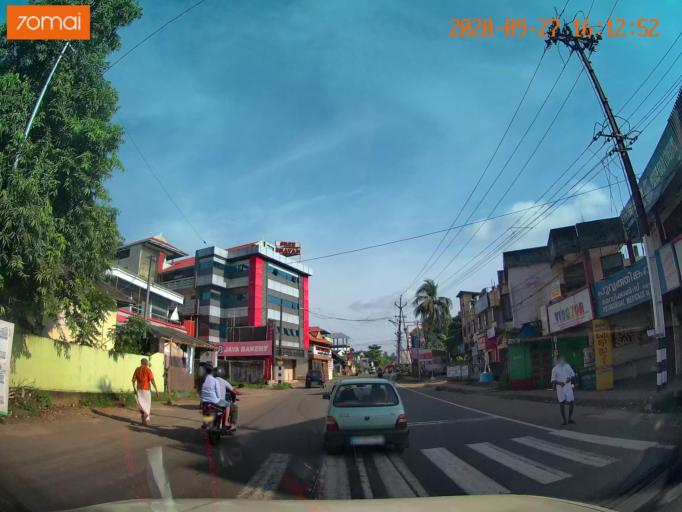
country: IN
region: Kerala
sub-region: Thrissur District
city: Trichur
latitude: 10.4739
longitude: 76.2413
